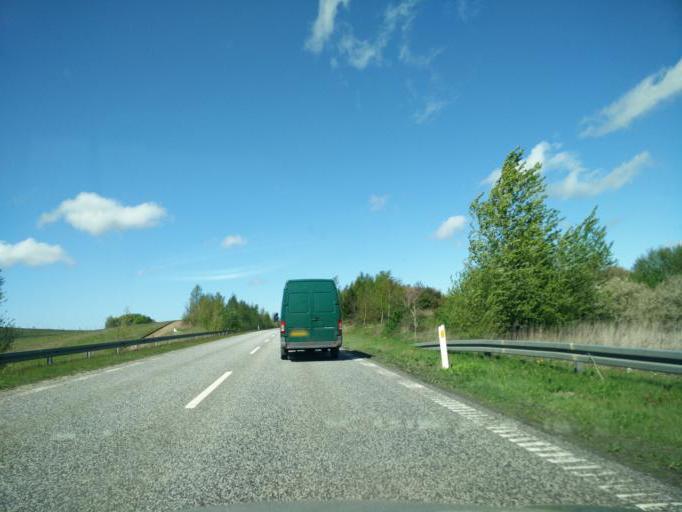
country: DK
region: Capital Region
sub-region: Hillerod Kommune
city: Hillerod
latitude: 55.9677
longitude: 12.2445
